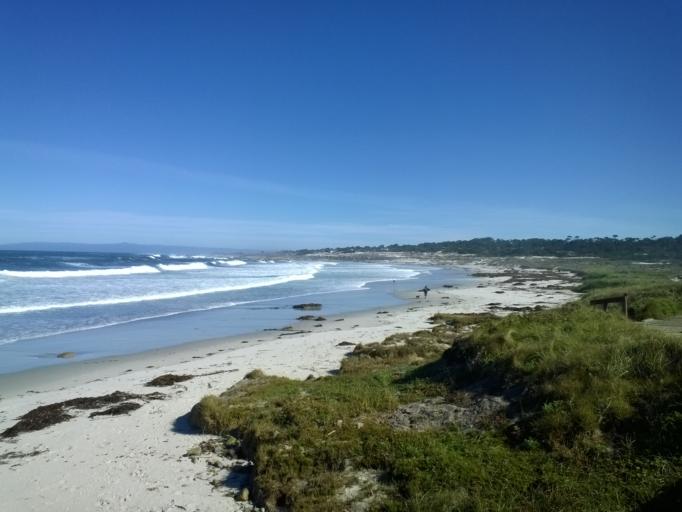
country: US
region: California
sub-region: Monterey County
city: Del Monte Forest
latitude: 36.6144
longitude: -121.9454
